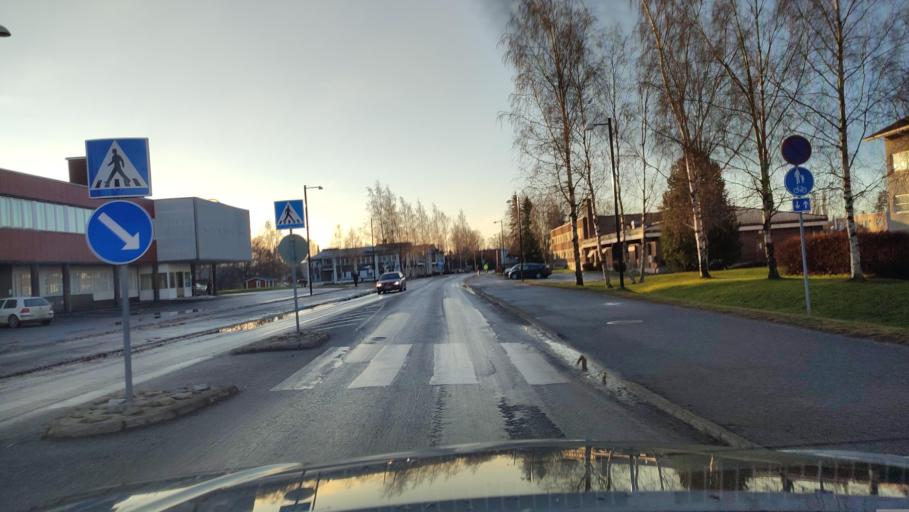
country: FI
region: Ostrobothnia
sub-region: Sydosterbotten
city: Naerpes
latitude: 62.4748
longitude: 21.3376
